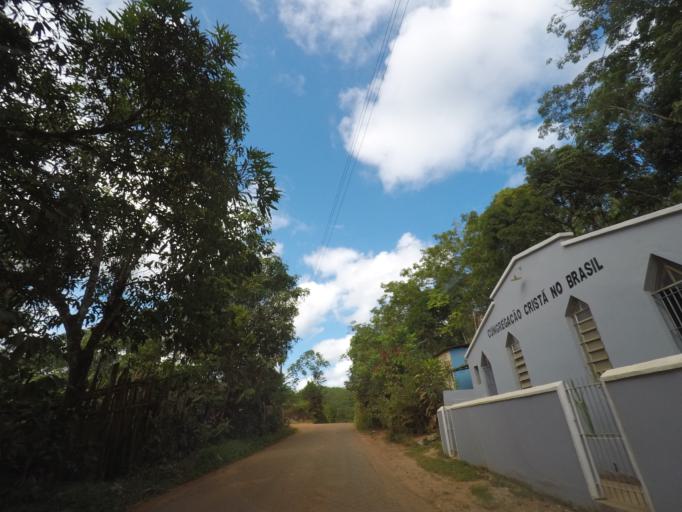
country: BR
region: Bahia
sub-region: Itacare
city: Itacare
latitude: -14.2249
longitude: -39.0935
